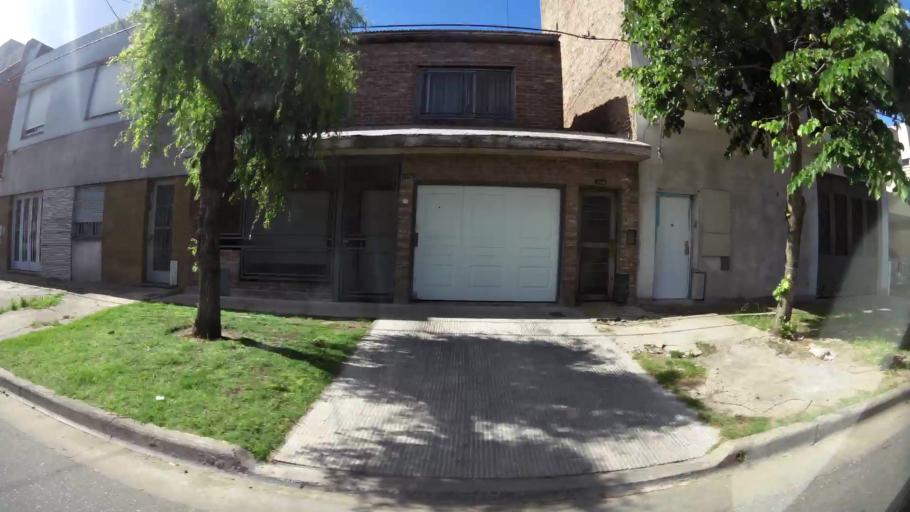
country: AR
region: Santa Fe
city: Granadero Baigorria
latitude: -32.9347
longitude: -60.7172
